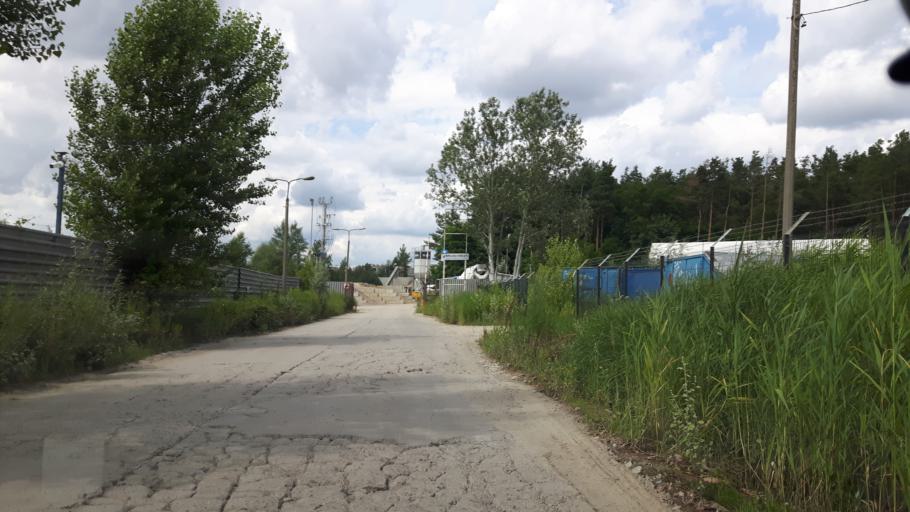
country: PL
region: Masovian Voivodeship
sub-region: Powiat wolominski
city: Zabki
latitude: 52.2723
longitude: 21.1234
